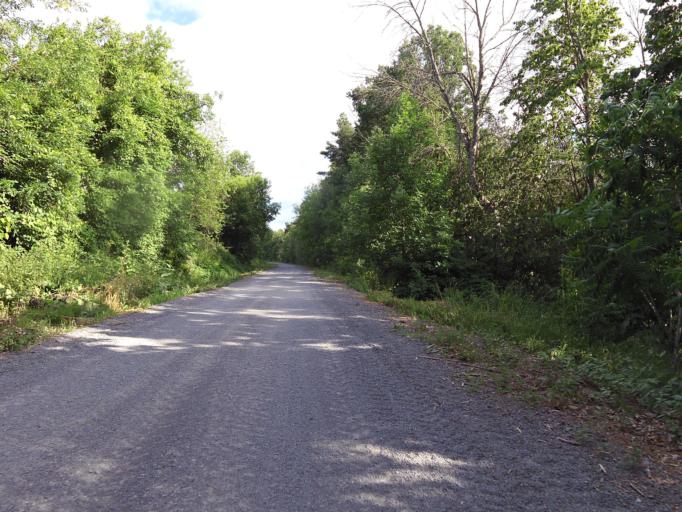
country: CA
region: Ontario
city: Arnprior
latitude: 45.3173
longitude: -76.2851
